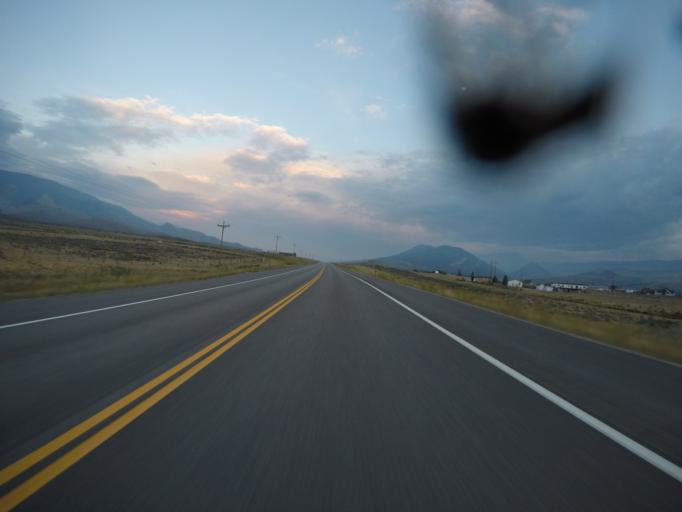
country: US
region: Colorado
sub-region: Grand County
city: Kremmling
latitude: 39.9337
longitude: -106.3427
